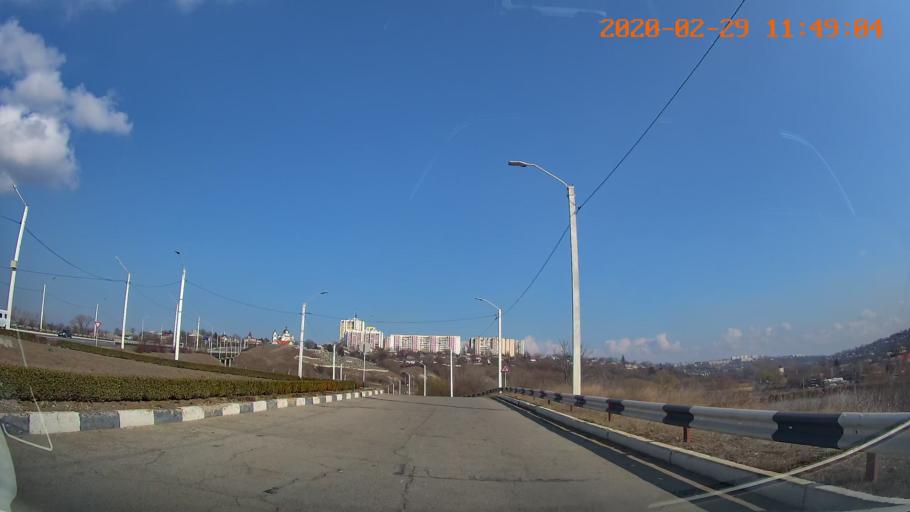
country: MD
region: Telenesti
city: Ribnita
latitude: 47.7527
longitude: 28.9942
